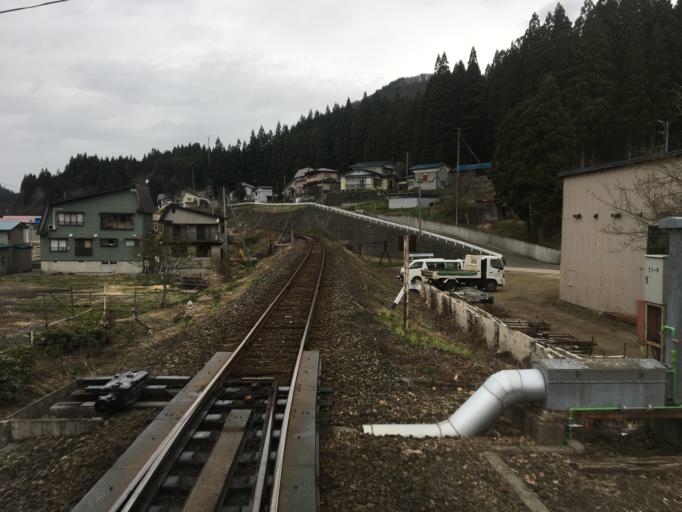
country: JP
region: Akita
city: Takanosu
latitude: 40.0625
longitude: 140.4180
